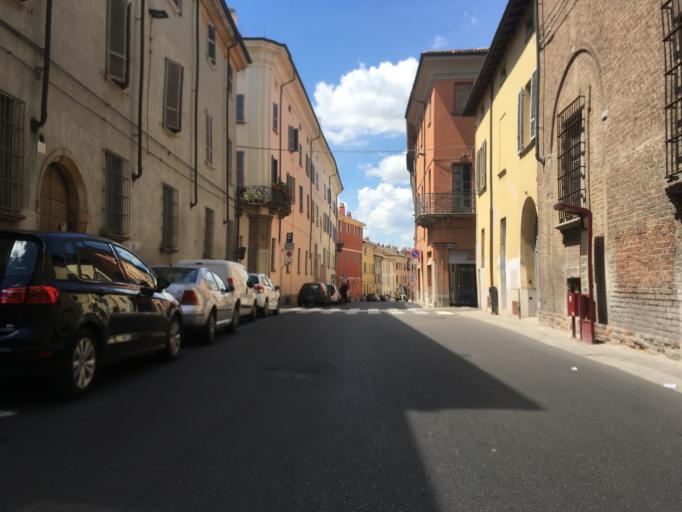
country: IT
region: Emilia-Romagna
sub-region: Provincia di Piacenza
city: Piacenza
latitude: 45.0559
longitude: 9.6915
